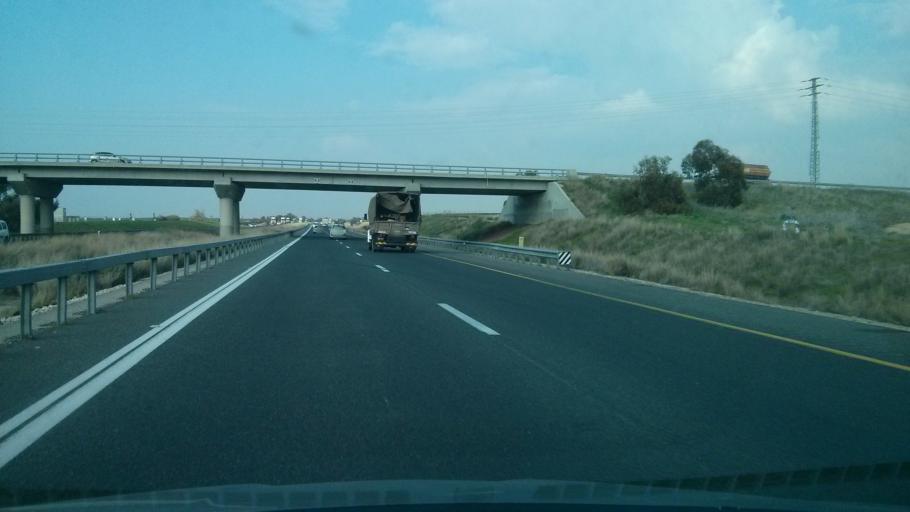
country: IL
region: Central District
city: Gedera
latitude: 31.7445
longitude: 34.8231
